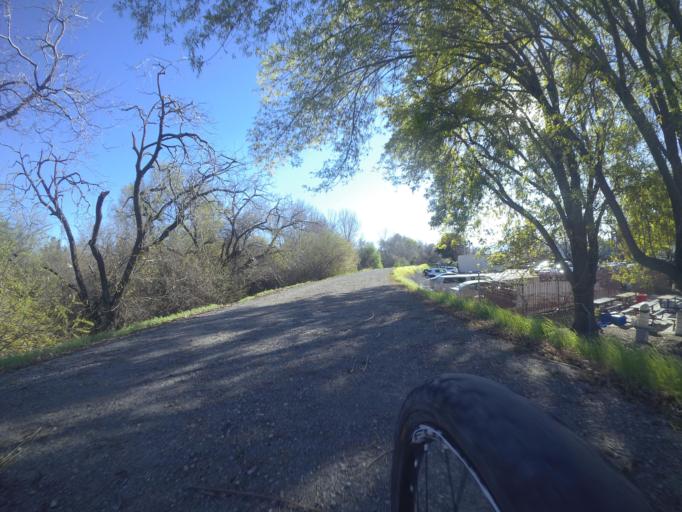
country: US
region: California
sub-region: Santa Clara County
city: Santa Clara
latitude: 37.3848
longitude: -121.9363
